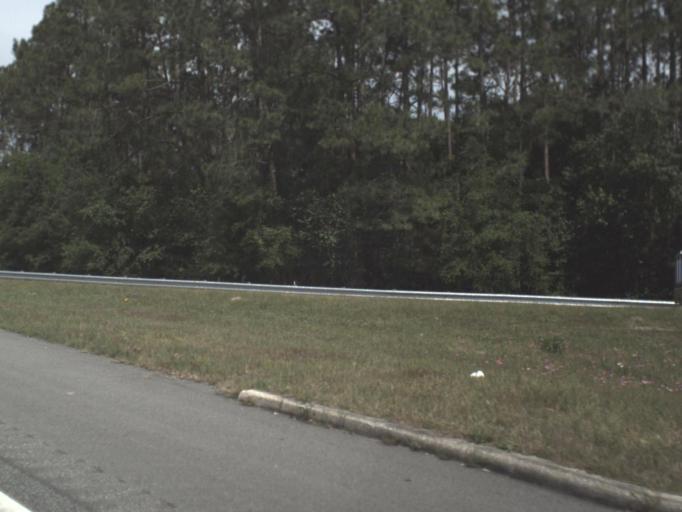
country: US
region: Florida
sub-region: Suwannee County
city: Live Oak
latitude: 30.3427
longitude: -83.0915
